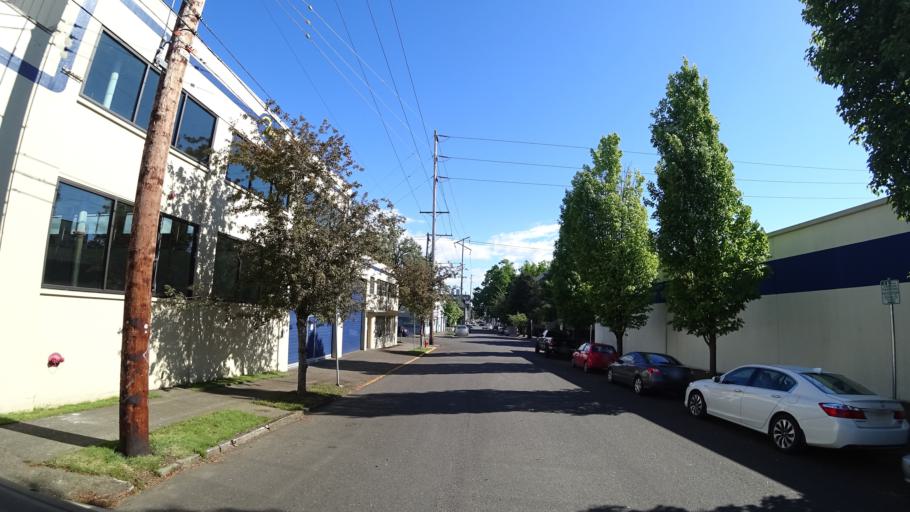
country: US
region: Oregon
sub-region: Multnomah County
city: Portland
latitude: 45.5254
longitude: -122.6566
